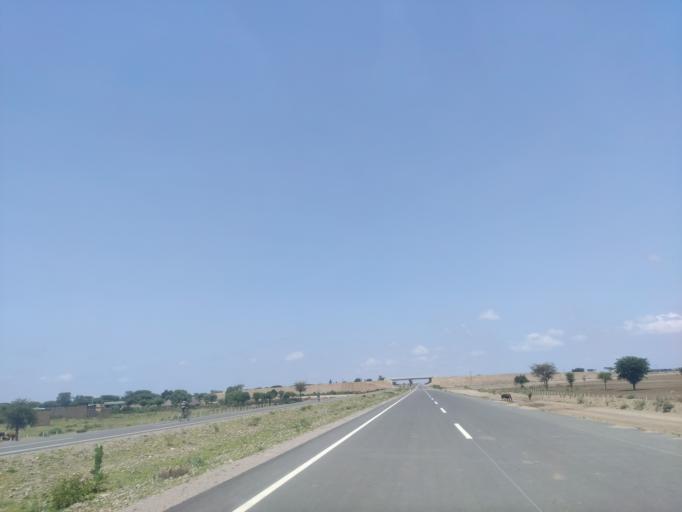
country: ET
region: Oromiya
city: Mojo
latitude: 8.3052
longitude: 38.9396
